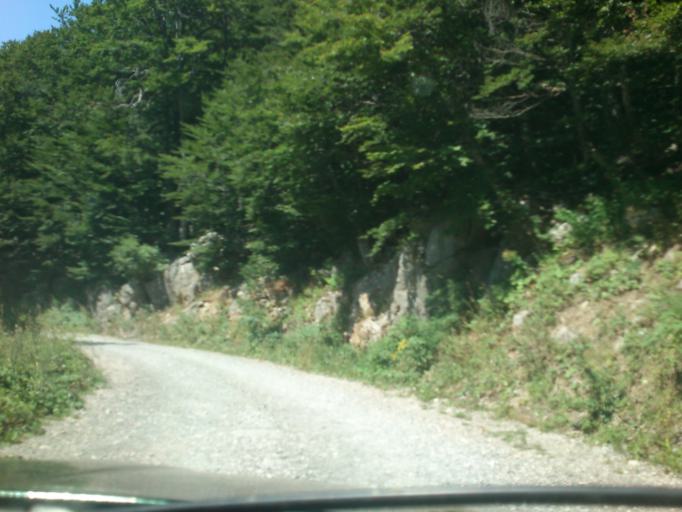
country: HR
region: Licko-Senjska
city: Senj
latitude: 44.8204
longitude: 14.9880
